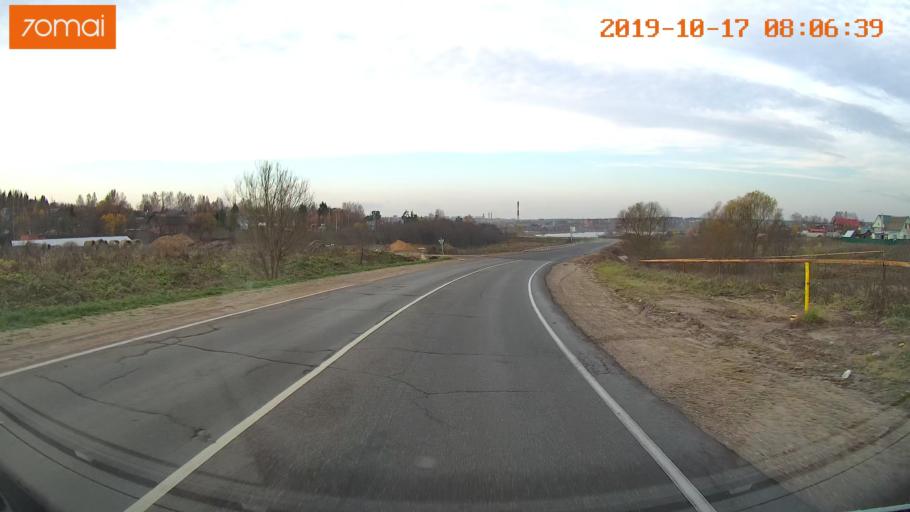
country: RU
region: Vladimir
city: Kol'chugino
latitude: 56.3202
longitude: 39.4116
